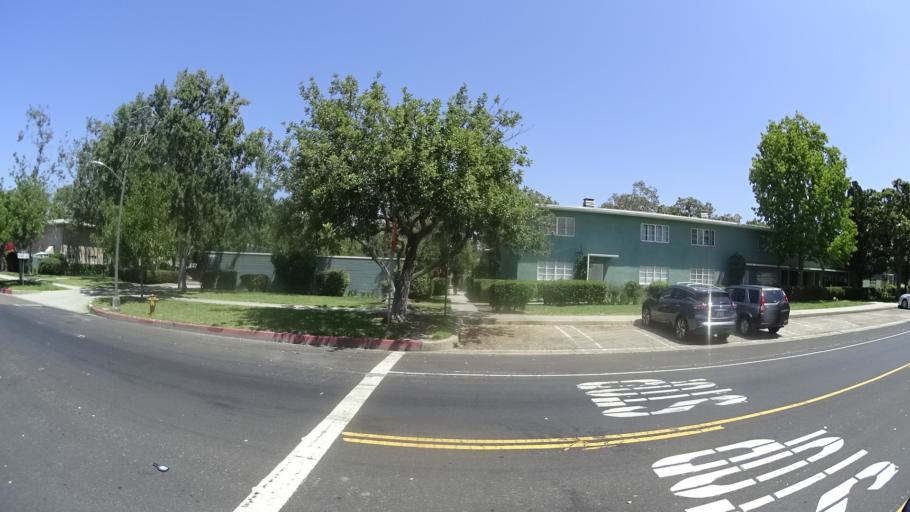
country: US
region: California
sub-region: Los Angeles County
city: Ladera Heights
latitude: 34.0182
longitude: -118.3630
